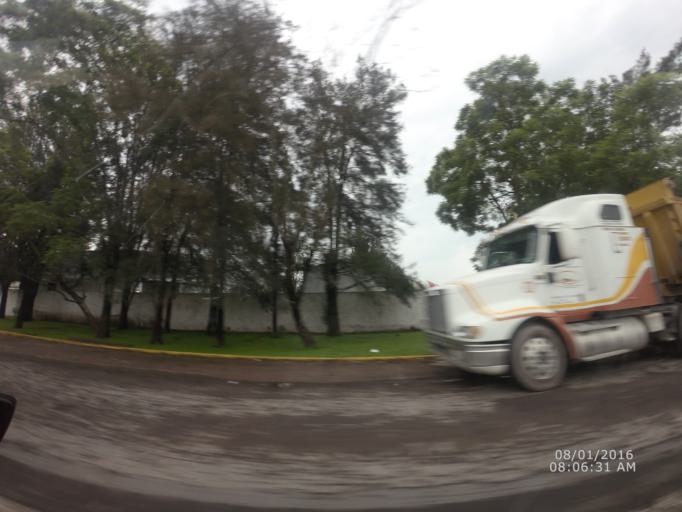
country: MX
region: Nayarit
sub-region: Tepic
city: La Corregidora
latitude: 21.4467
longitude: -104.8177
